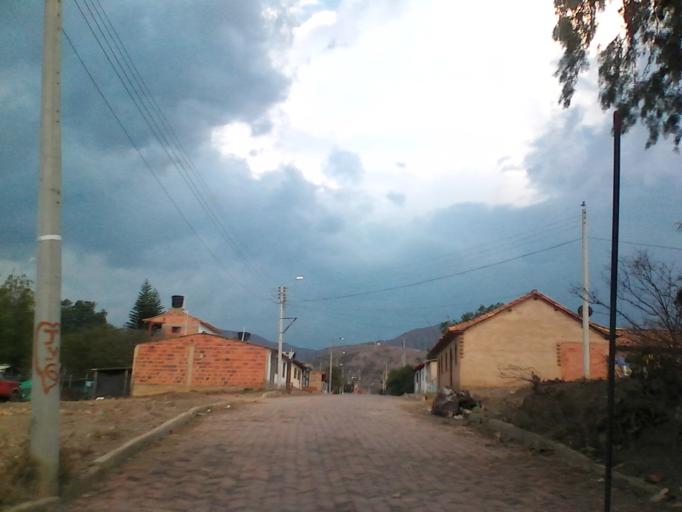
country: CO
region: Boyaca
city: Sachica
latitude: 5.5830
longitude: -73.5393
